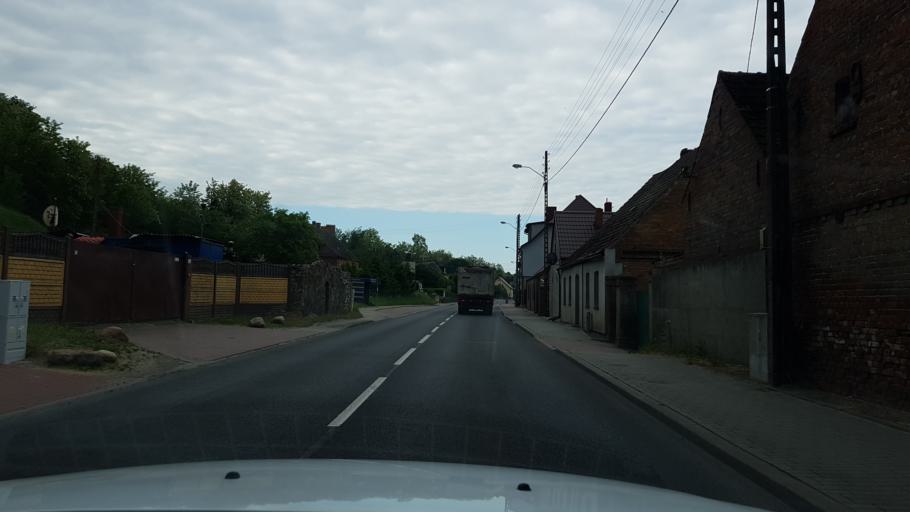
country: PL
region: West Pomeranian Voivodeship
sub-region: Powiat gryfinski
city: Gryfino
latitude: 53.2884
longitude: 14.5181
